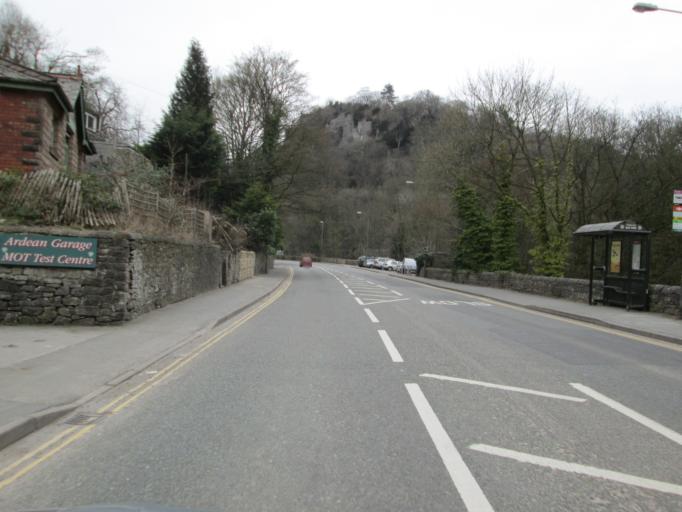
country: GB
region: England
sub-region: Derbyshire
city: Cromford
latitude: 53.1225
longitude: -1.5581
